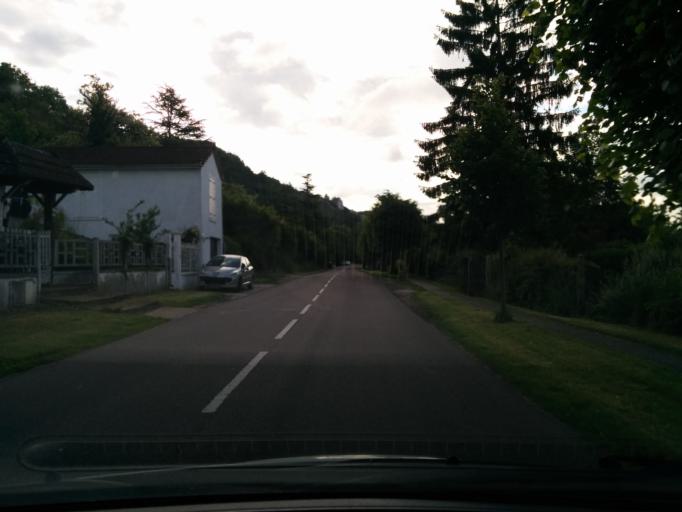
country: FR
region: Haute-Normandie
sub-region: Departement de l'Eure
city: Gasny
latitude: 49.0843
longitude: 1.6497
